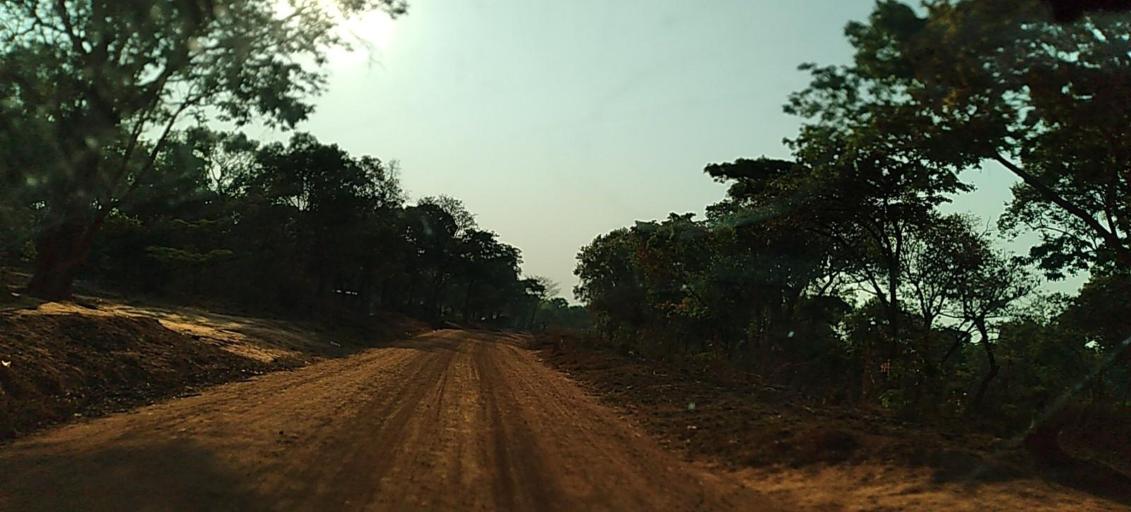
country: ZM
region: North-Western
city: Kasempa
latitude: -13.4721
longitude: 25.8715
